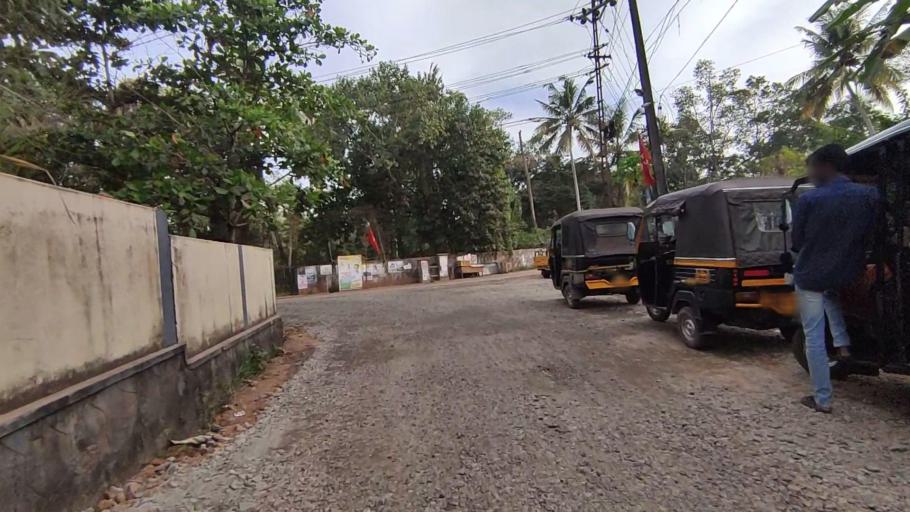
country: IN
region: Kerala
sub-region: Kottayam
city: Kottayam
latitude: 9.6095
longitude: 76.4870
